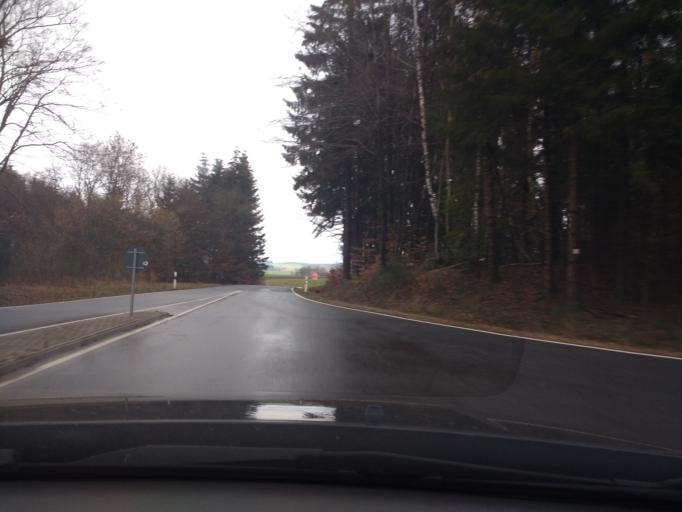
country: DE
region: Rheinland-Pfalz
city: Mandern
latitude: 49.5936
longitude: 6.7714
